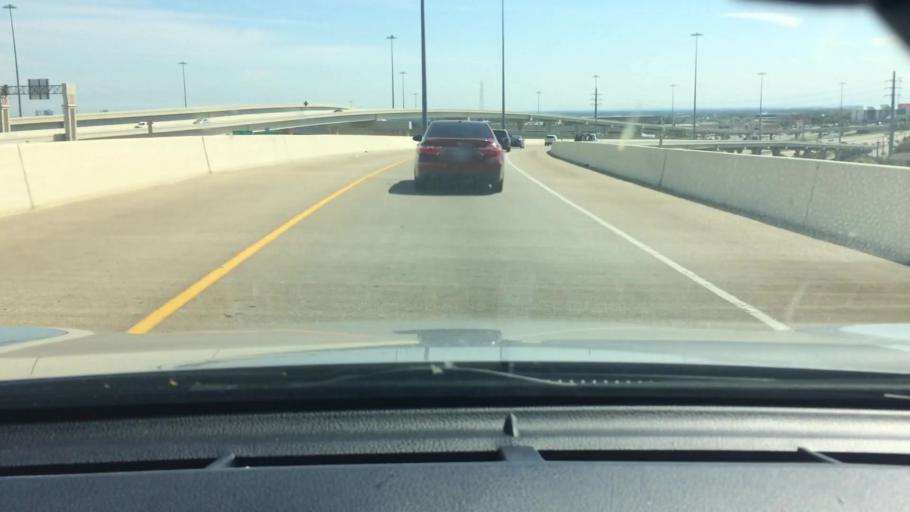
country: US
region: Texas
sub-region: Bexar County
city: Balcones Heights
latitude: 29.5028
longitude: -98.5500
